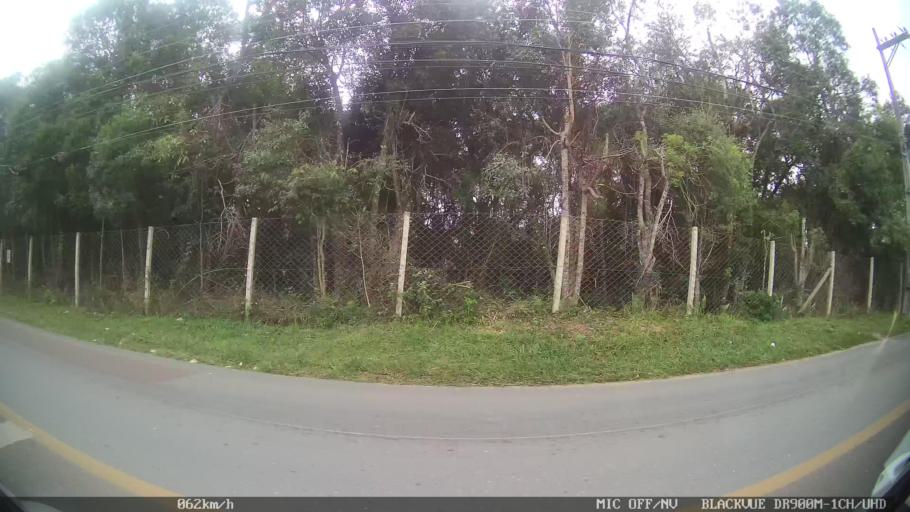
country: BR
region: Parana
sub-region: Almirante Tamandare
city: Almirante Tamandare
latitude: -25.3614
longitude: -49.2717
